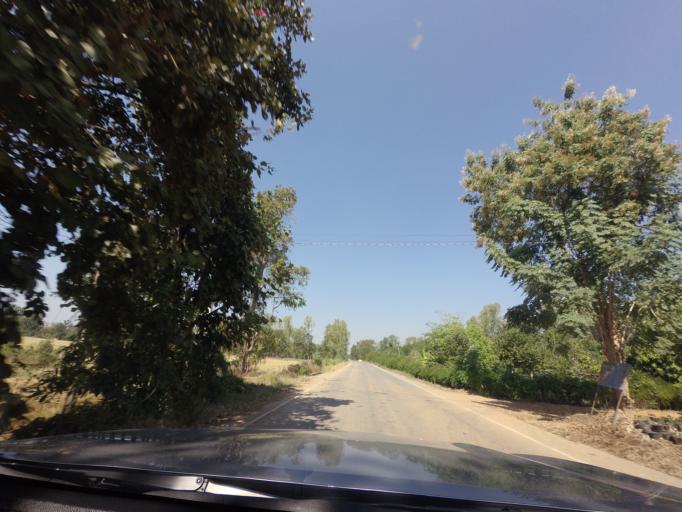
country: TH
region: Sukhothai
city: Si Samrong
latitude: 17.1434
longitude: 99.7702
